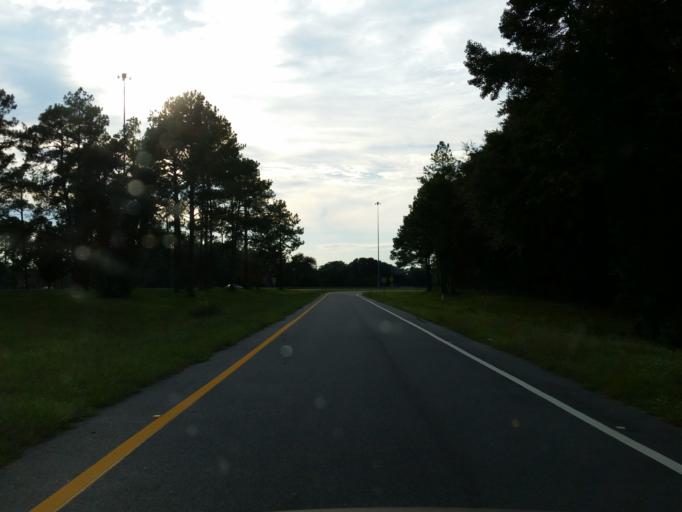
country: US
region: Georgia
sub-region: Echols County
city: Statenville
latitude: 30.5964
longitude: -83.1194
